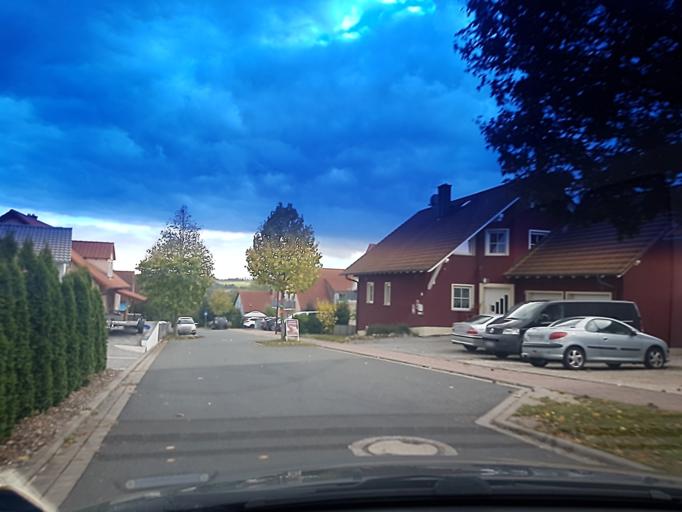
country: DE
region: Bavaria
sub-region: Regierungsbezirk Mittelfranken
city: Burghaslach
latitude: 49.7363
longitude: 10.6090
